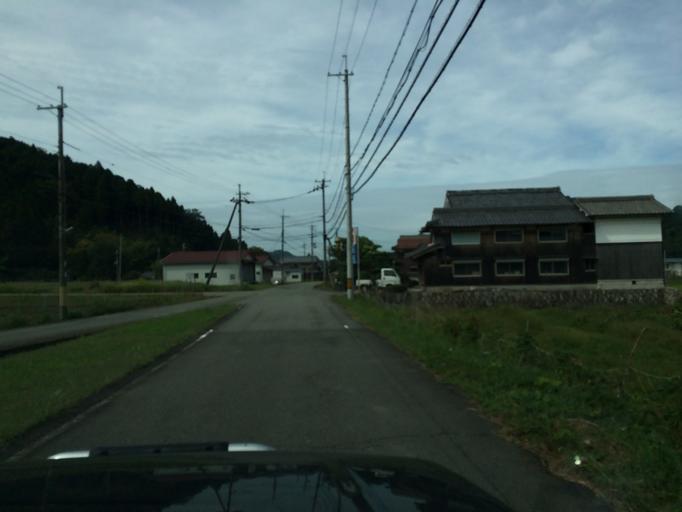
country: JP
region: Hyogo
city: Sasayama
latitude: 35.0720
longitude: 135.3577
